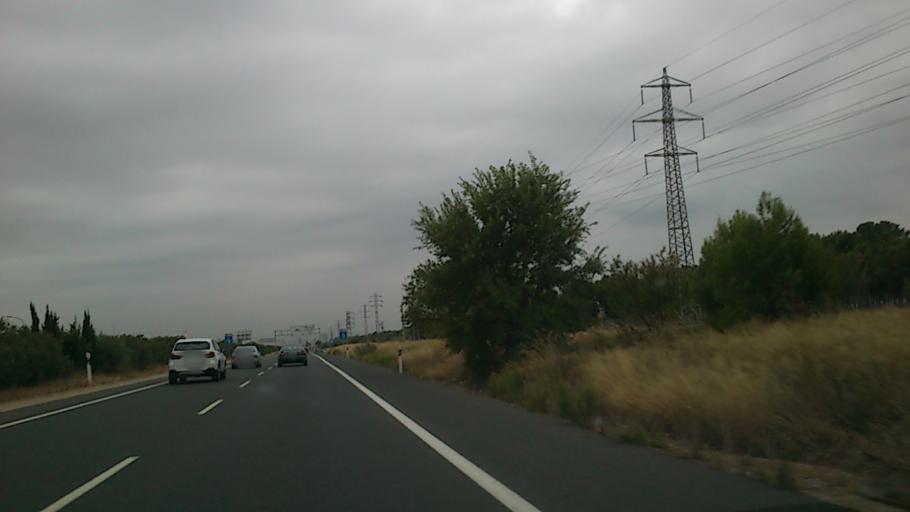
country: ES
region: Aragon
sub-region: Provincia de Zaragoza
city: Villanueva de Gallego
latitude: 41.7242
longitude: -0.8536
